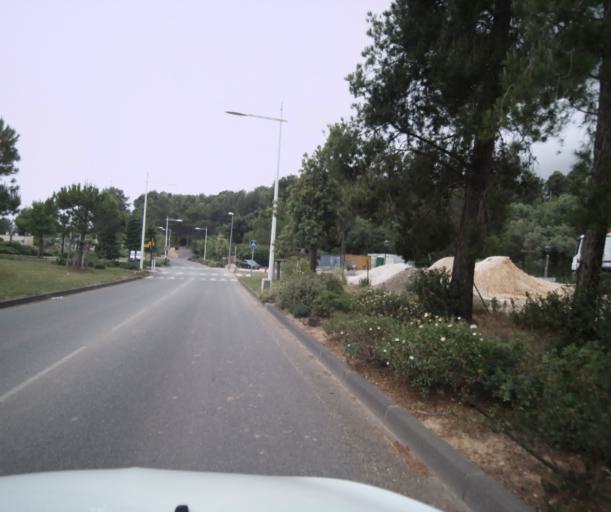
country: FR
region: Provence-Alpes-Cote d'Azur
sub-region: Departement du Var
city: La Garde
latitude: 43.1224
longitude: 5.9922
